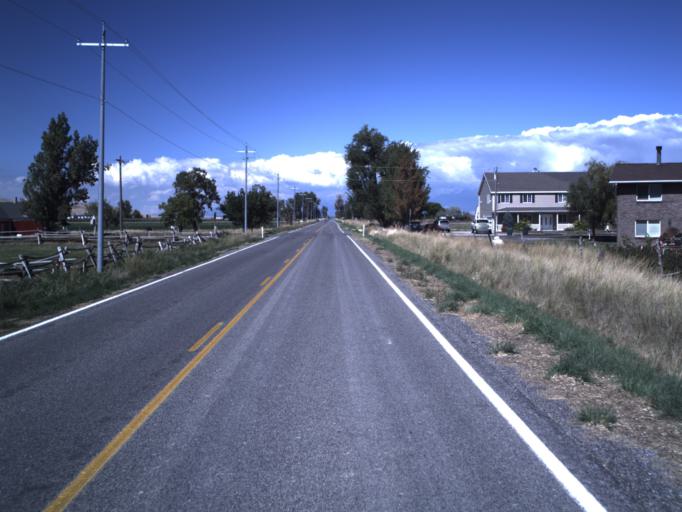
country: US
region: Utah
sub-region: Utah County
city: West Mountain
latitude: 40.0769
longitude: -111.7878
